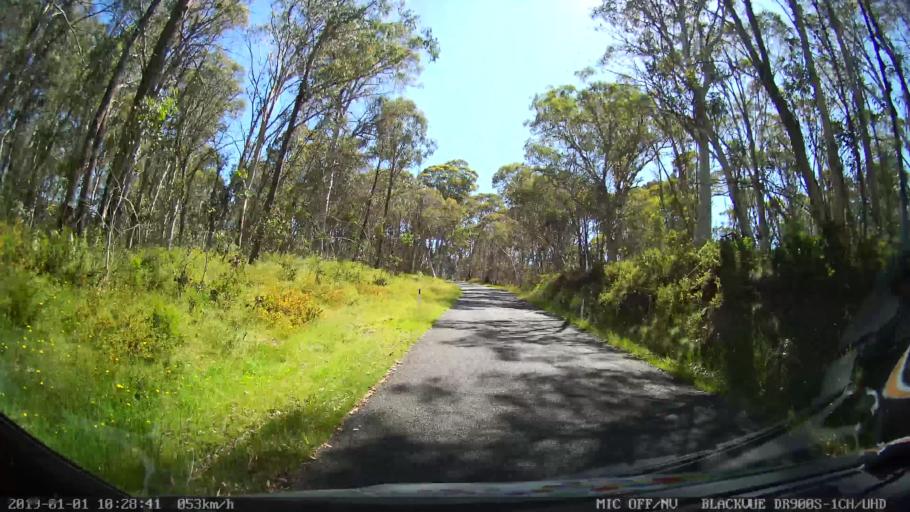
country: AU
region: New South Wales
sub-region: Snowy River
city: Jindabyne
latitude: -36.0588
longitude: 148.2425
